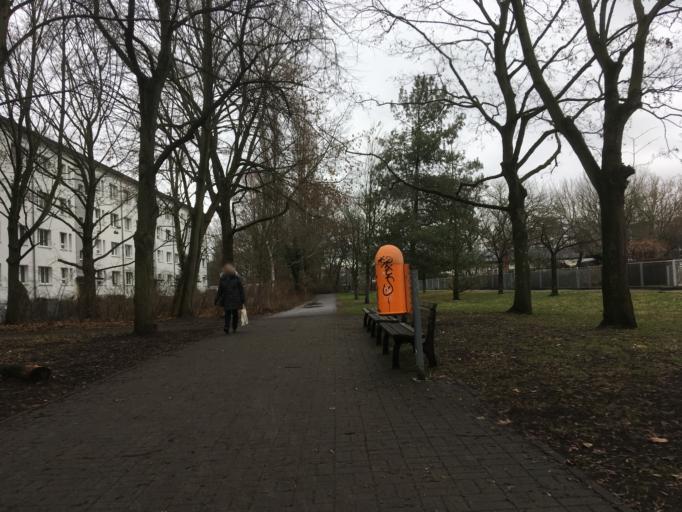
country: DE
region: Berlin
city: Friedrichsfelde
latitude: 52.5000
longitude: 13.5135
